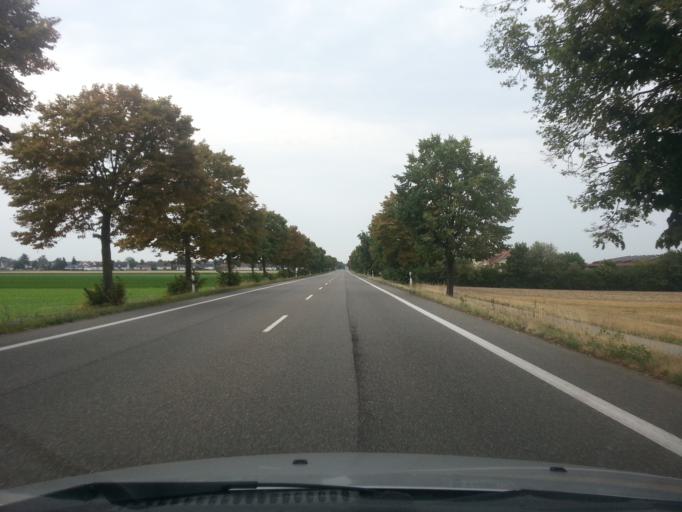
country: DE
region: Rheinland-Pfalz
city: Bobenheim-Roxheim
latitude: 49.6006
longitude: 8.3576
